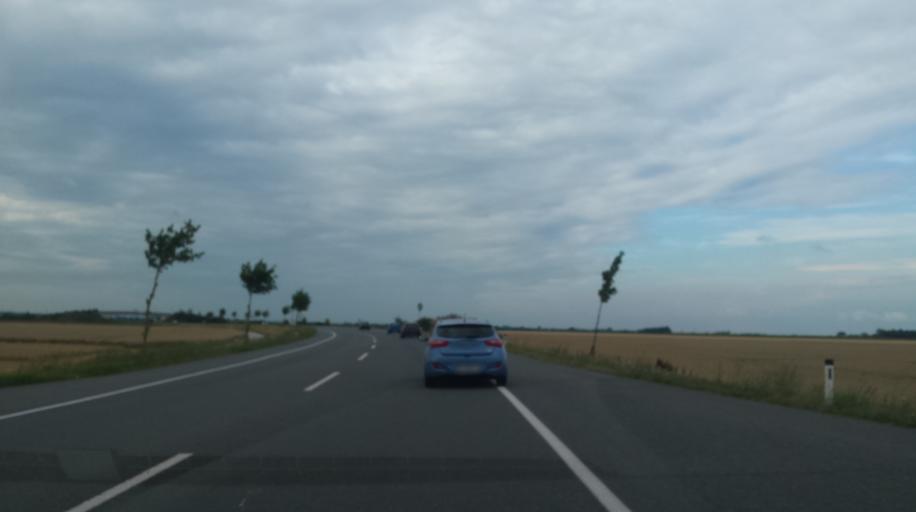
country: AT
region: Lower Austria
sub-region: Politischer Bezirk Wien-Umgebung
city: Himberg
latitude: 48.0754
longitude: 16.4616
